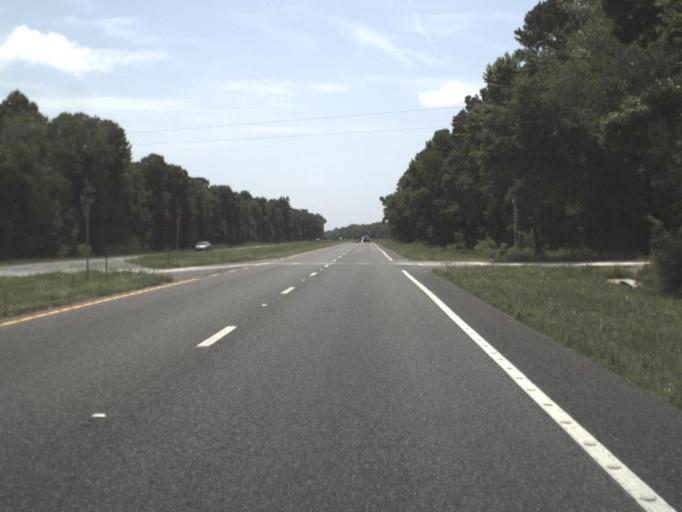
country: US
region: Florida
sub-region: Taylor County
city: Perry
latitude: 29.9708
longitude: -83.4800
